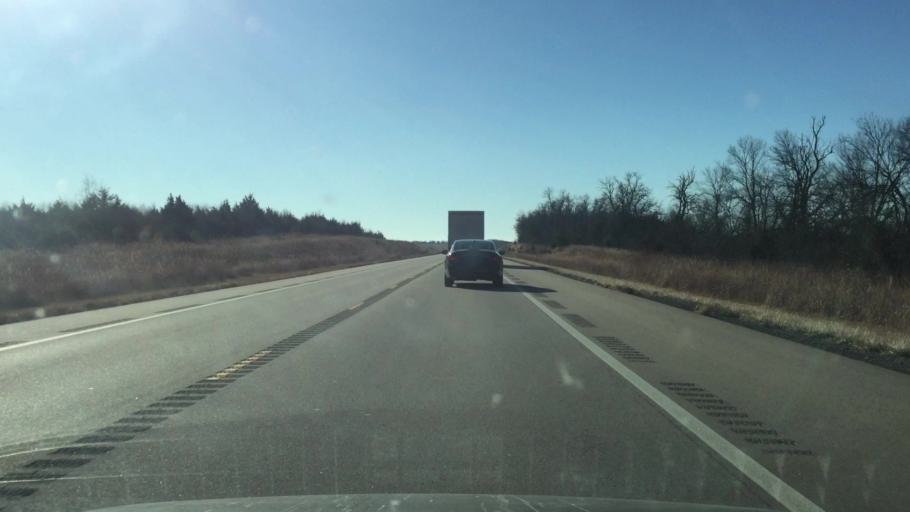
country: US
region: Kansas
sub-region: Allen County
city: Iola
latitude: 38.0347
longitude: -95.3806
